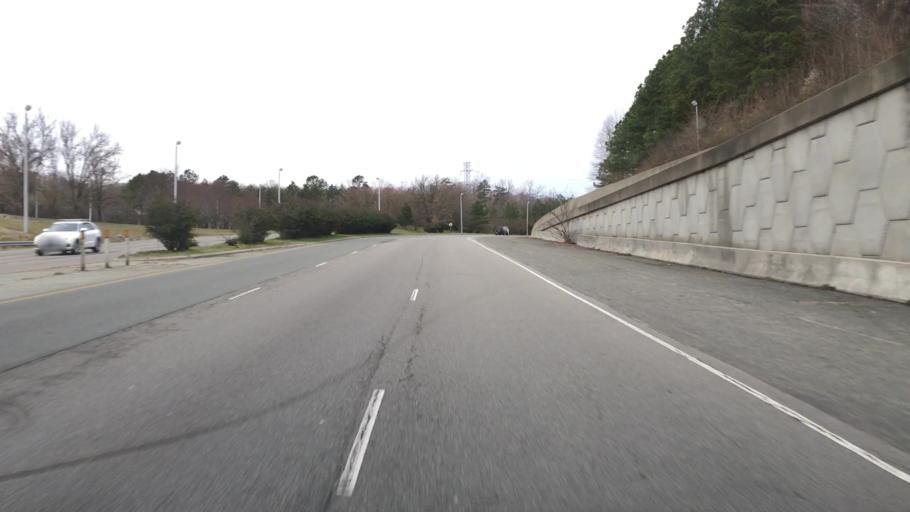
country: US
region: Virginia
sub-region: Chesterfield County
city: Bon Air
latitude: 37.5455
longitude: -77.5534
